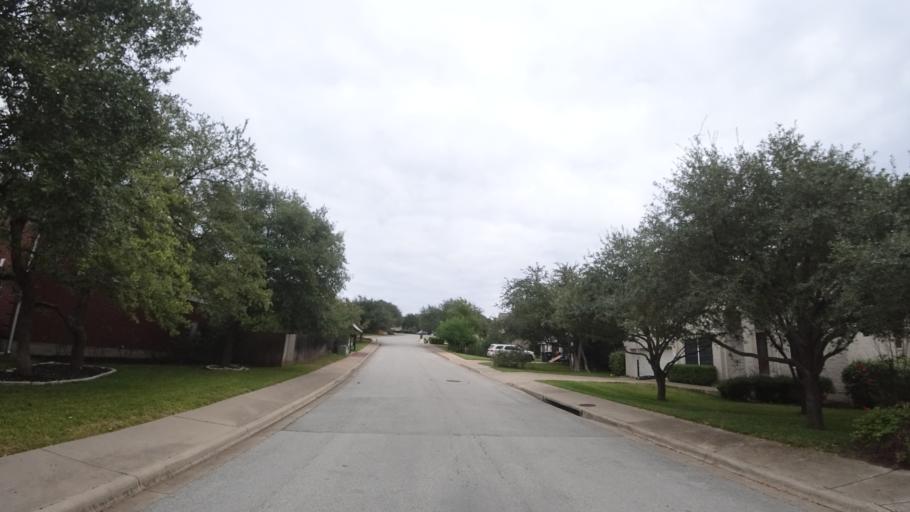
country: US
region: Texas
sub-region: Travis County
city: Bee Cave
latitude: 30.3156
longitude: -97.9194
